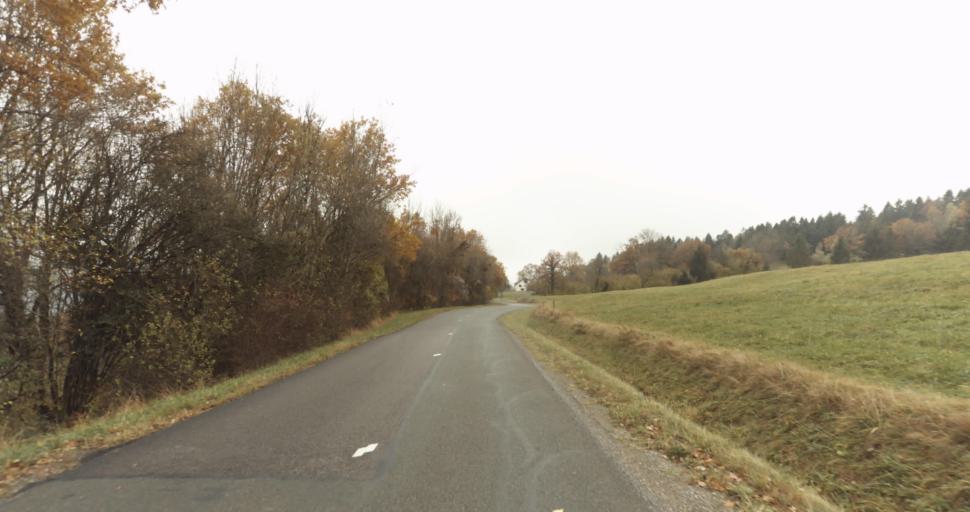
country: FR
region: Rhone-Alpes
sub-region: Departement de la Haute-Savoie
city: Groisy
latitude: 46.0227
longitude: 6.1791
